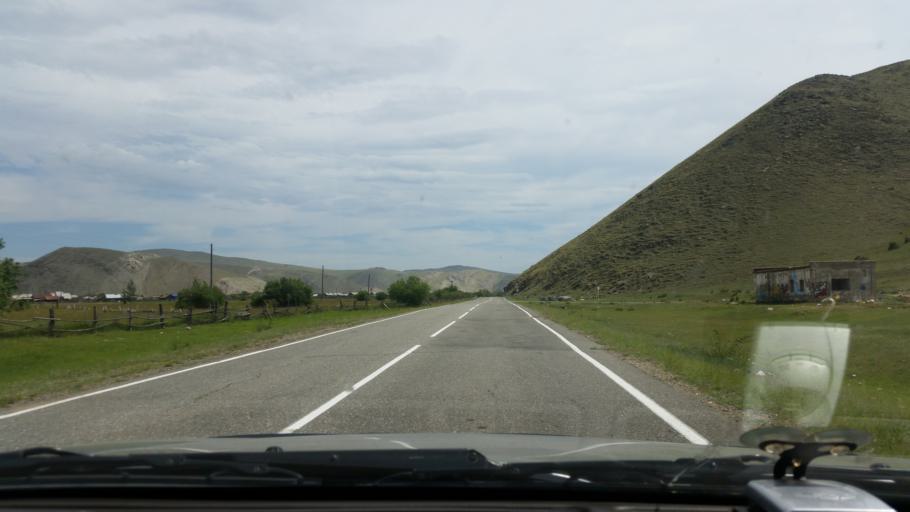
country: RU
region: Irkutsk
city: Yelantsy
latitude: 52.8064
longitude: 106.4588
